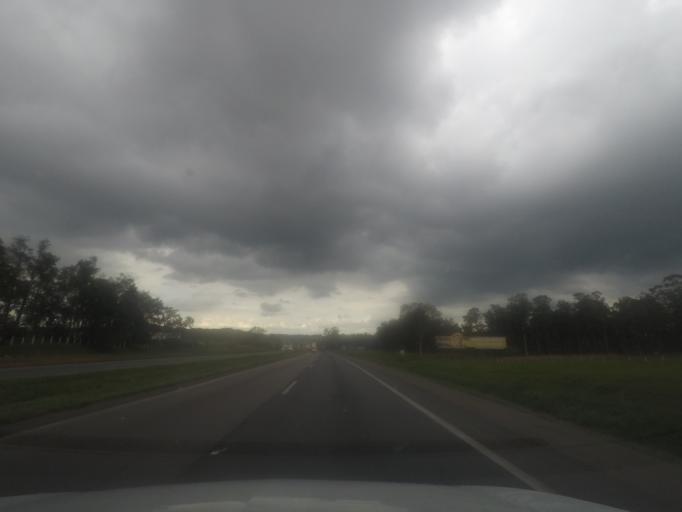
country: BR
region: Parana
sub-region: Sao Jose Dos Pinhais
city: Sao Jose dos Pinhais
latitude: -25.5619
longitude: -49.2611
